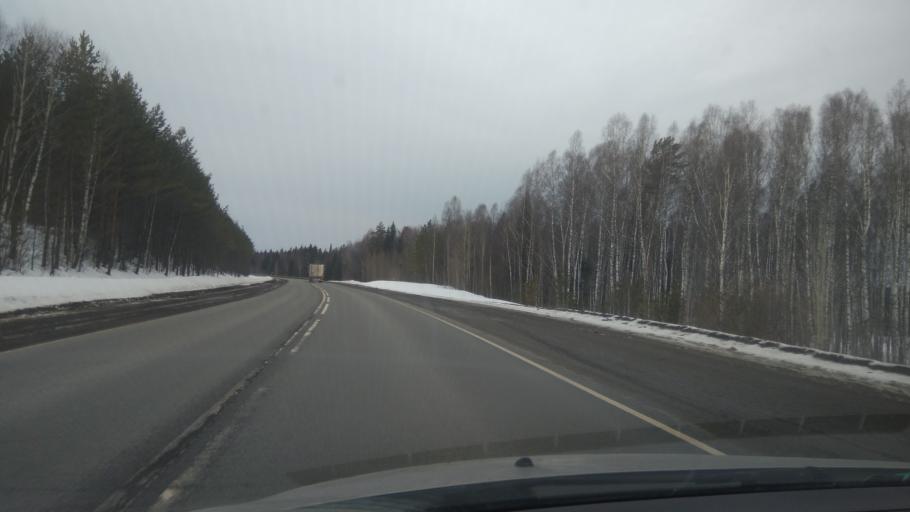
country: RU
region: Sverdlovsk
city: Ufimskiy
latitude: 56.7858
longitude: 58.3899
